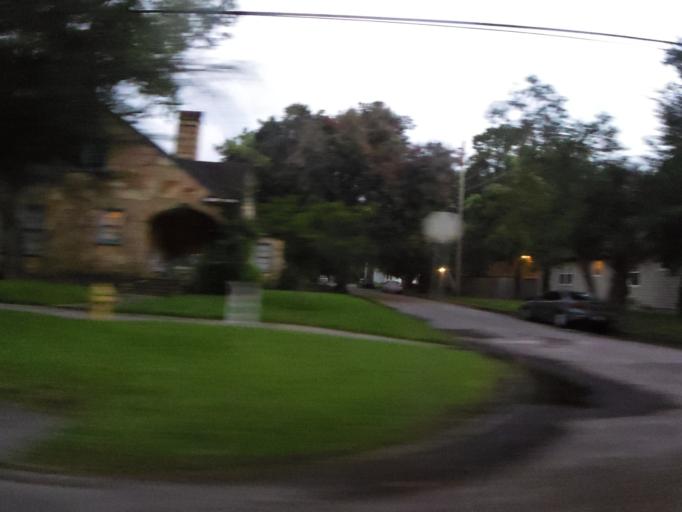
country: US
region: Florida
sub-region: Duval County
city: Jacksonville
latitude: 30.3132
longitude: -81.7019
